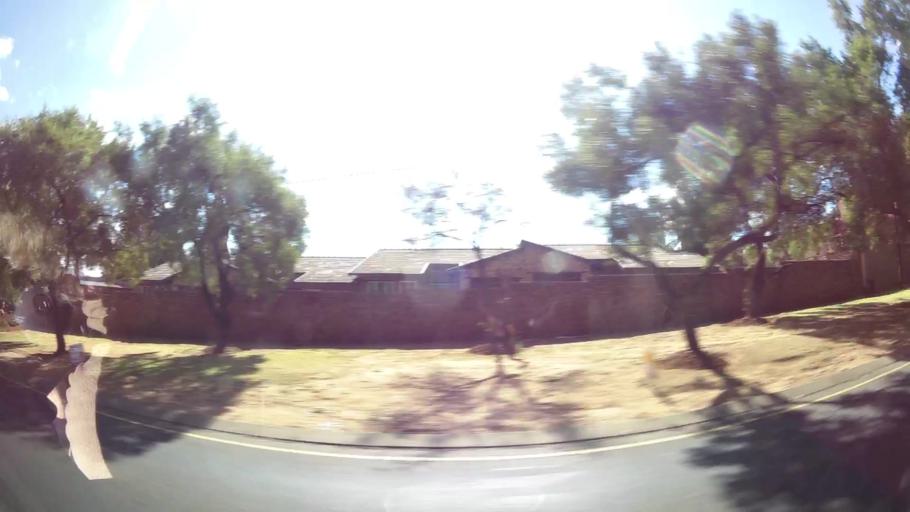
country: ZA
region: Gauteng
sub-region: City of Johannesburg Metropolitan Municipality
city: Roodepoort
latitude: -26.1044
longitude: 27.8445
